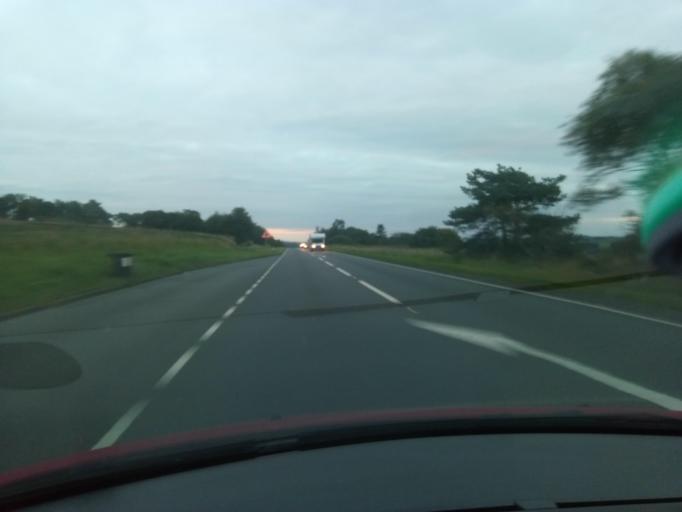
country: GB
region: England
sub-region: Northumberland
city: Bardon Mill
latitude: 54.9720
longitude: -2.3897
